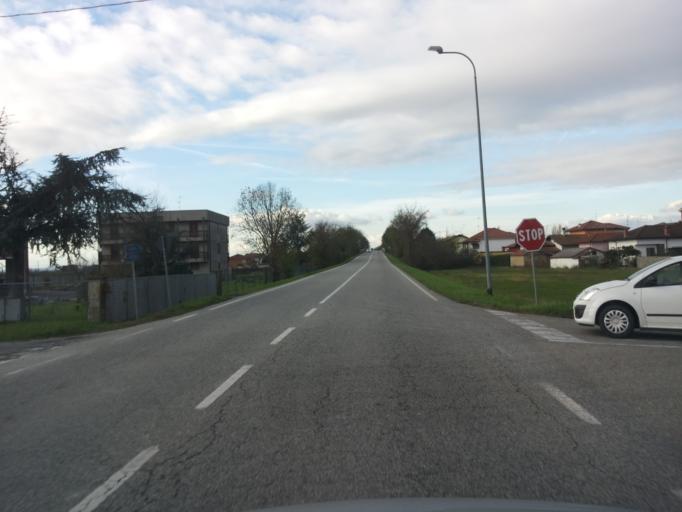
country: IT
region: Piedmont
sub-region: Provincia di Vercelli
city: Tronzano Vercellese
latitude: 45.3389
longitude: 8.1705
